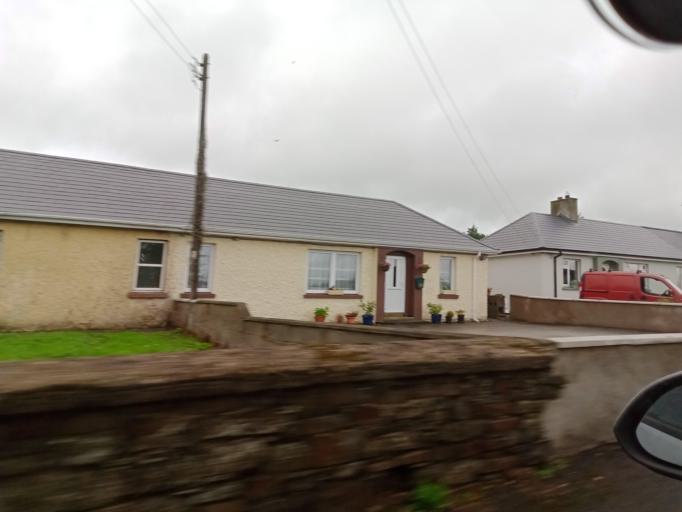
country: IE
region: Leinster
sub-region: Kilkenny
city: Castlecomer
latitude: 52.8287
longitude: -7.2033
